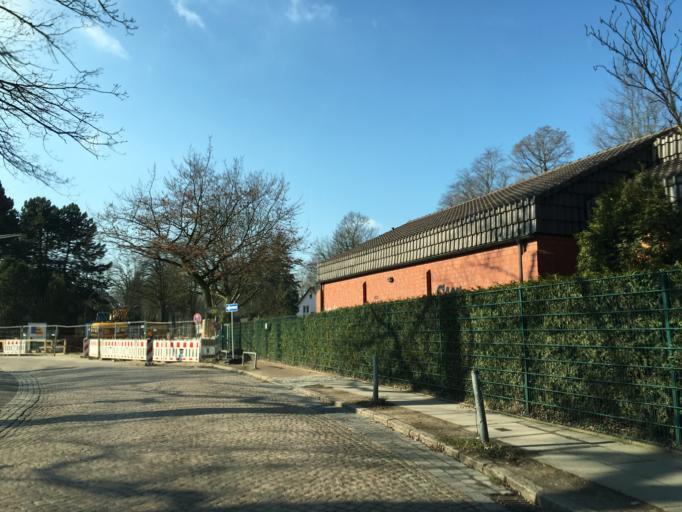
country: DE
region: Hamburg
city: Eidelstedt
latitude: 53.5578
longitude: 9.8594
